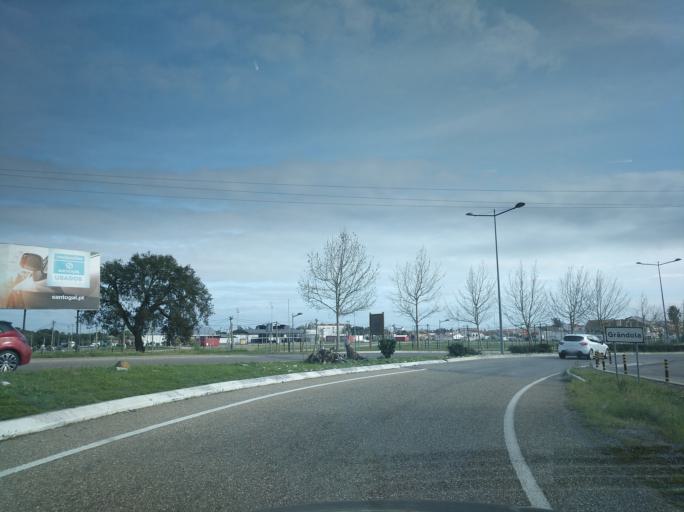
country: PT
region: Setubal
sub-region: Grandola
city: Grandola
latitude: 38.1862
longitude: -8.5682
